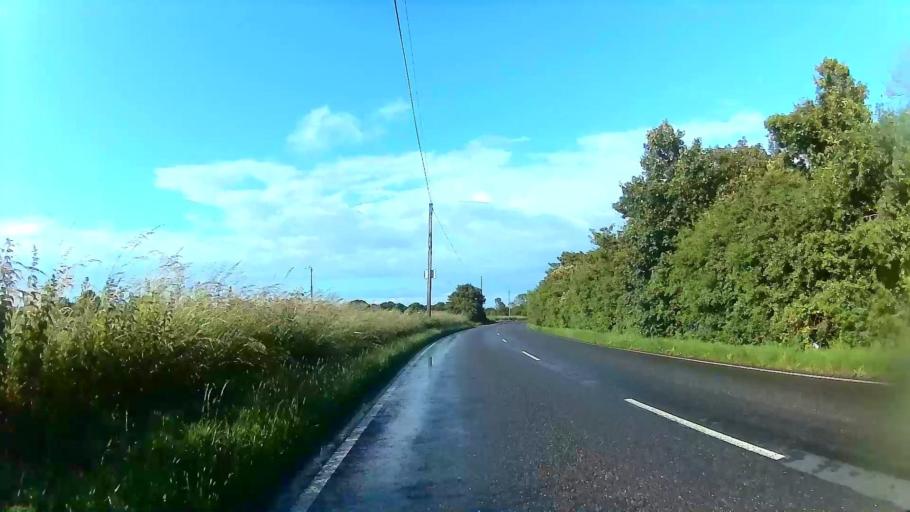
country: GB
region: England
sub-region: Essex
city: Writtle
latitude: 51.7218
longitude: 0.4022
